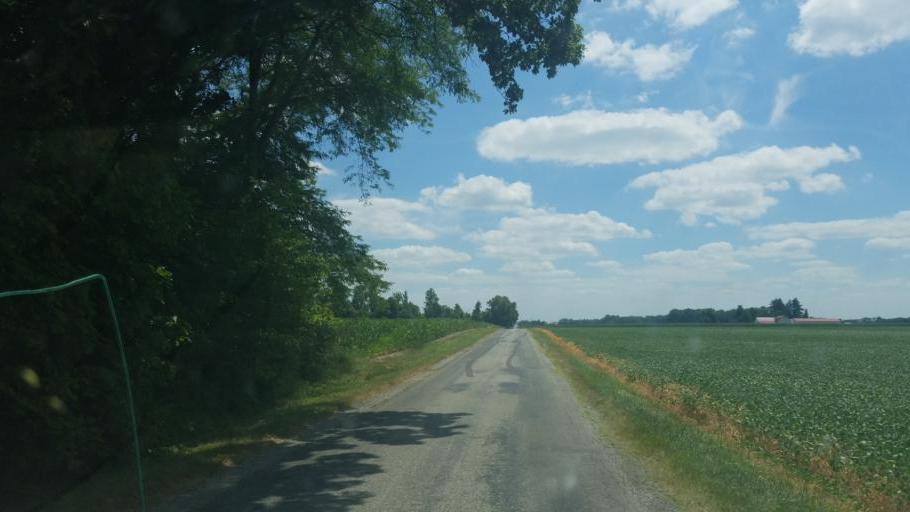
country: US
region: Ohio
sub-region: Defiance County
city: Hicksville
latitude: 41.3513
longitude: -84.6901
